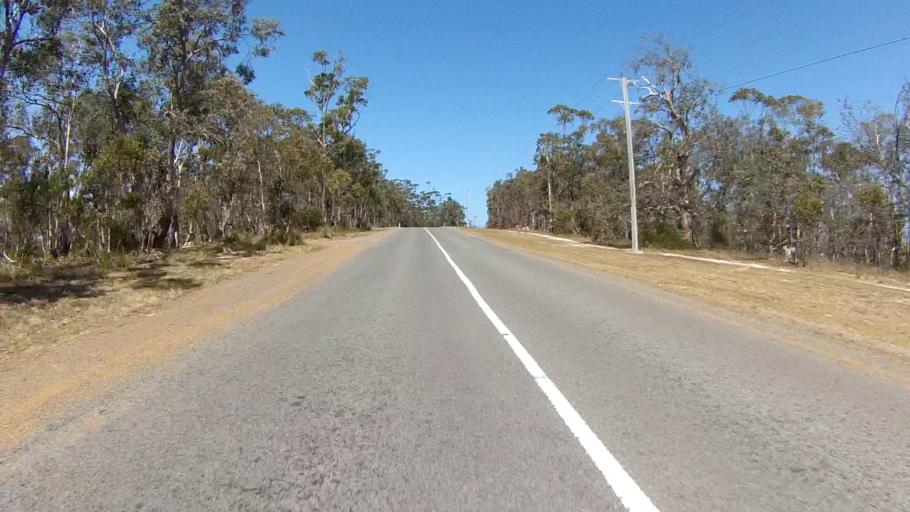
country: AU
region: Tasmania
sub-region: Clarence
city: Sandford
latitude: -43.0031
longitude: 147.4767
